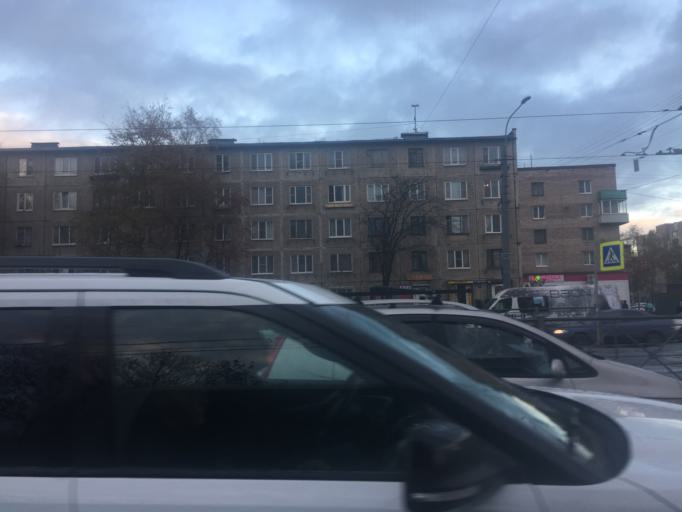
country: RU
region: St.-Petersburg
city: Obukhovo
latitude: 59.8824
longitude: 30.4691
